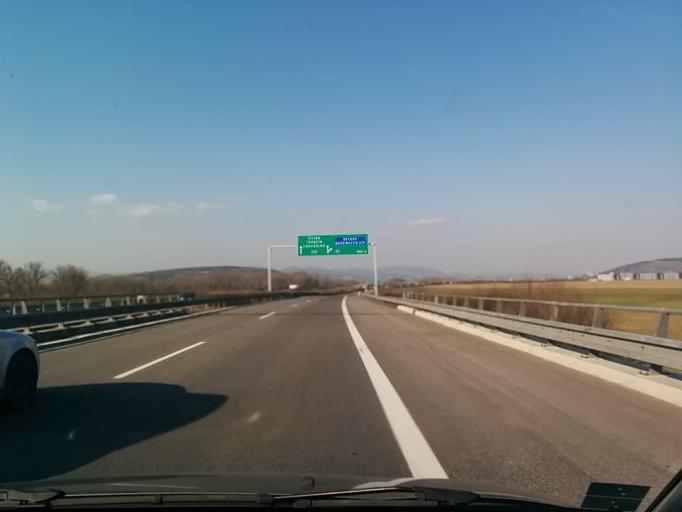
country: SK
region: Trenciansky
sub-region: Okres Nove Mesto nad Vahom
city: Nove Mesto nad Vahom
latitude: 48.7483
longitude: 17.8604
